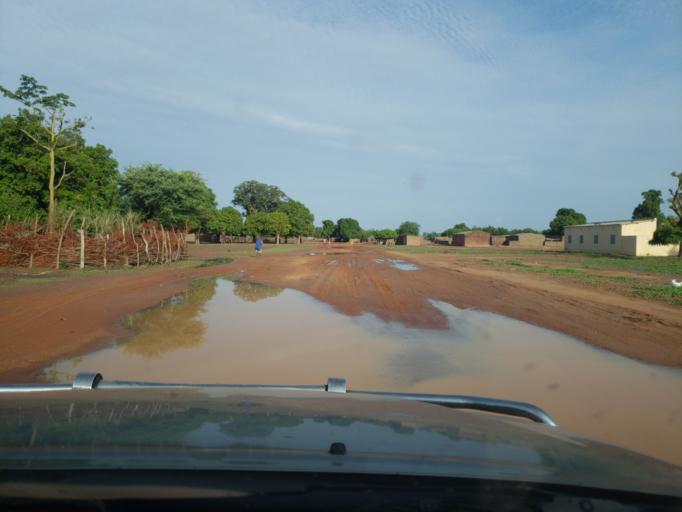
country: ML
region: Sikasso
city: Koutiala
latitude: 12.4228
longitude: -5.6809
